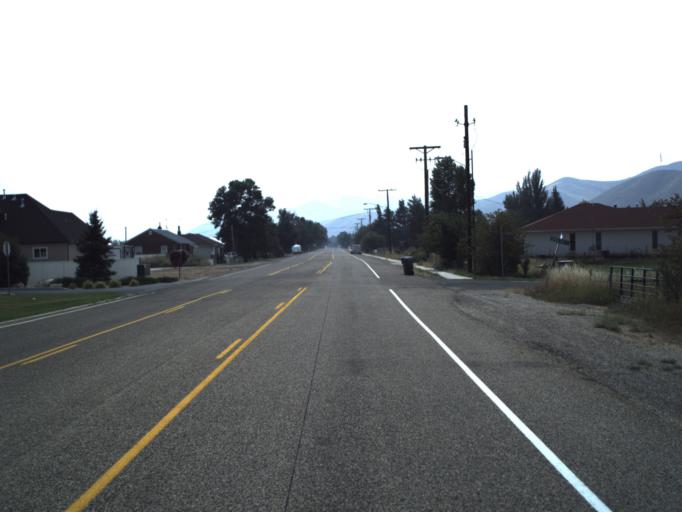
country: US
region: Utah
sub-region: Summit County
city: Coalville
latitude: 41.0244
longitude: -111.5040
